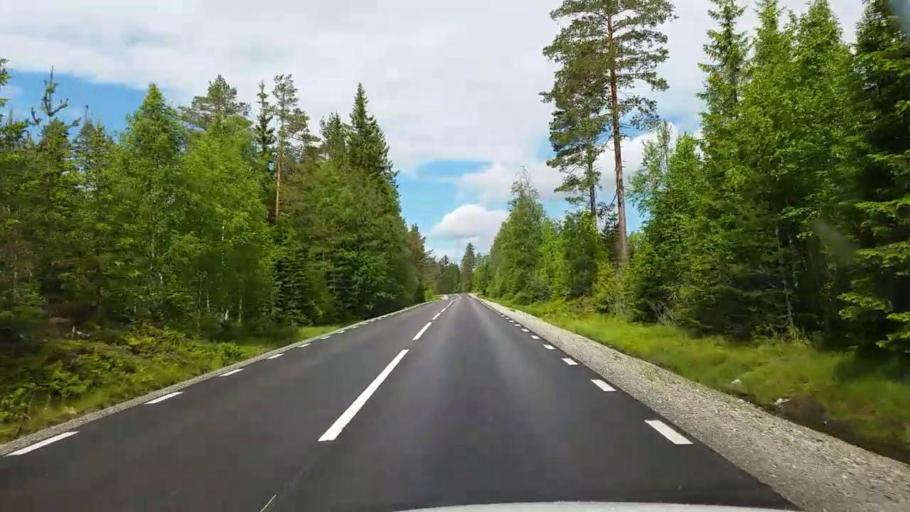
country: SE
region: Gaevleborg
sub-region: Sandvikens Kommun
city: Jarbo
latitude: 60.8840
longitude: 16.3841
